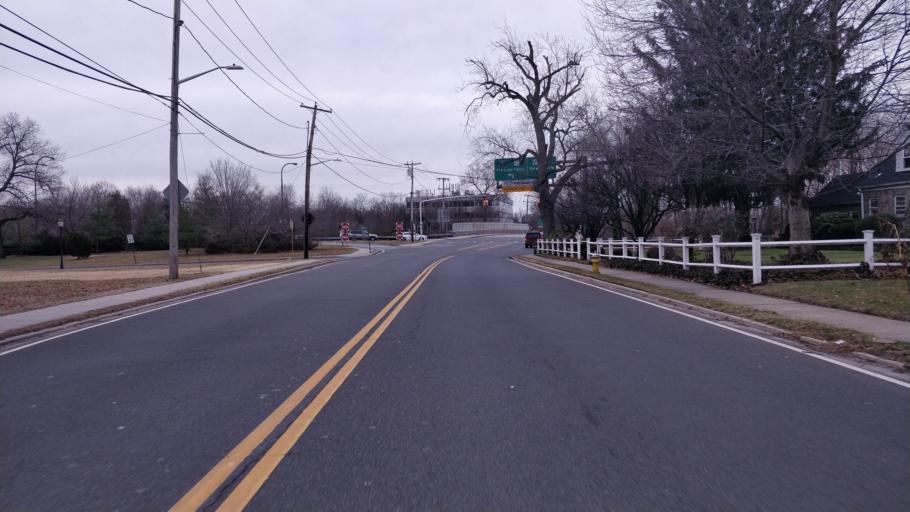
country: US
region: New York
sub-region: Nassau County
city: Westbury
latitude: 40.7651
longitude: -73.5871
